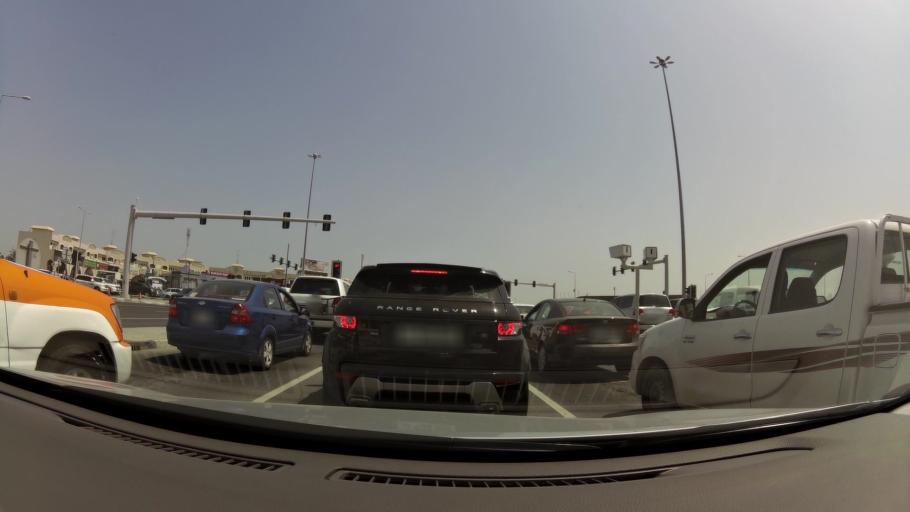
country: QA
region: Baladiyat ad Dawhah
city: Doha
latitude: 25.3223
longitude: 51.4859
